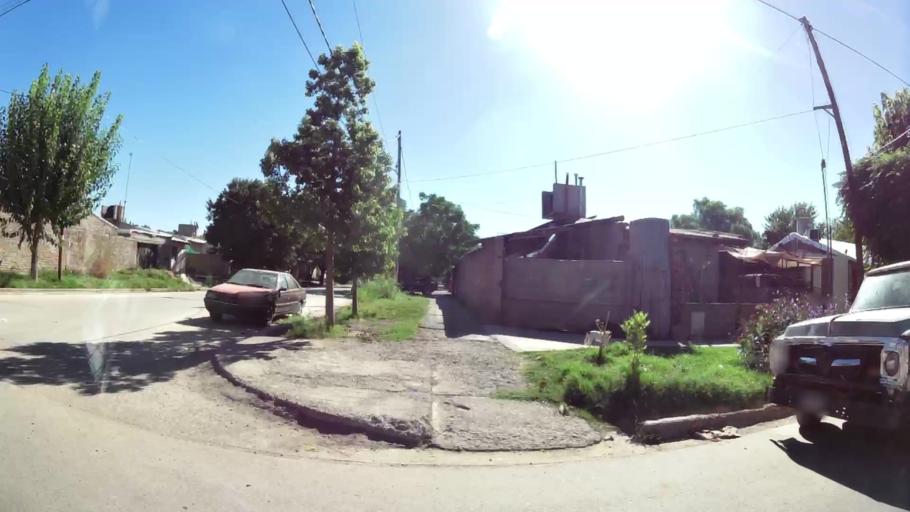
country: AR
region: Mendoza
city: Las Heras
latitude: -32.8471
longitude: -68.8241
